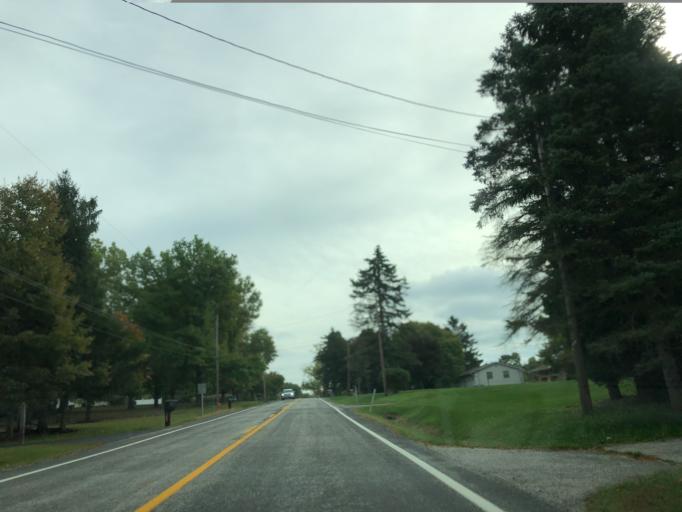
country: US
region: Ohio
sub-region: Summit County
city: Macedonia
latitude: 41.2924
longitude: -81.5430
